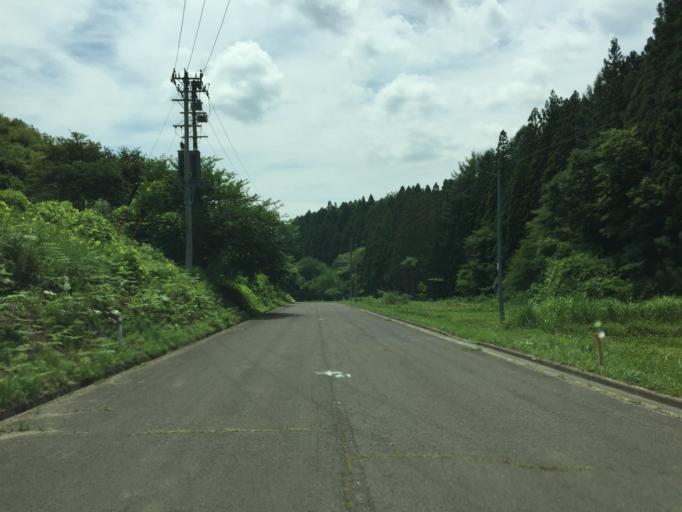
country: JP
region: Fukushima
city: Funehikimachi-funehiki
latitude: 37.6231
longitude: 140.6629
